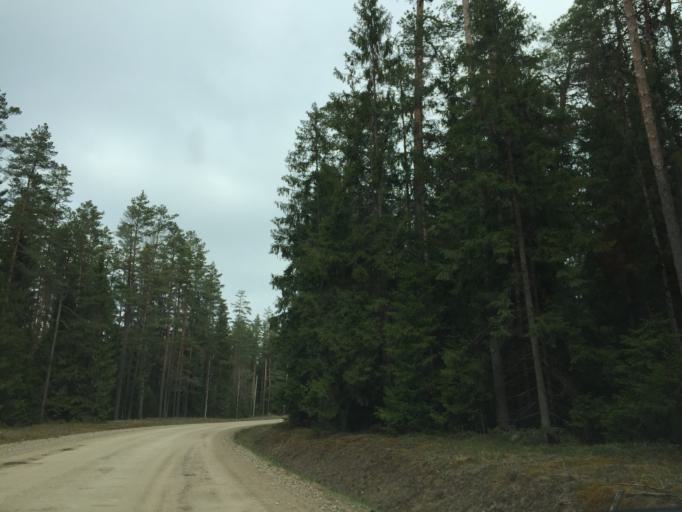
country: EE
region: Valgamaa
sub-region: Valga linn
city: Valga
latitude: 57.5890
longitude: 26.2201
